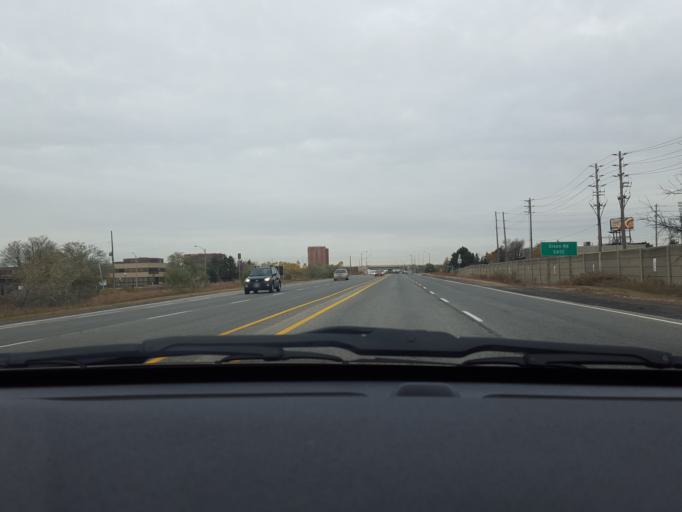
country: CA
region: Ontario
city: Etobicoke
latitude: 43.6840
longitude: -79.5803
